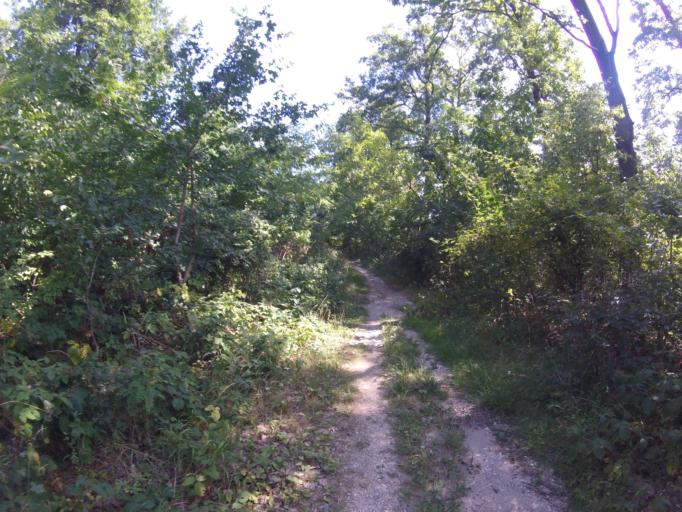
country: HU
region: Pest
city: Csobanka
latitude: 47.6874
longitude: 18.9853
